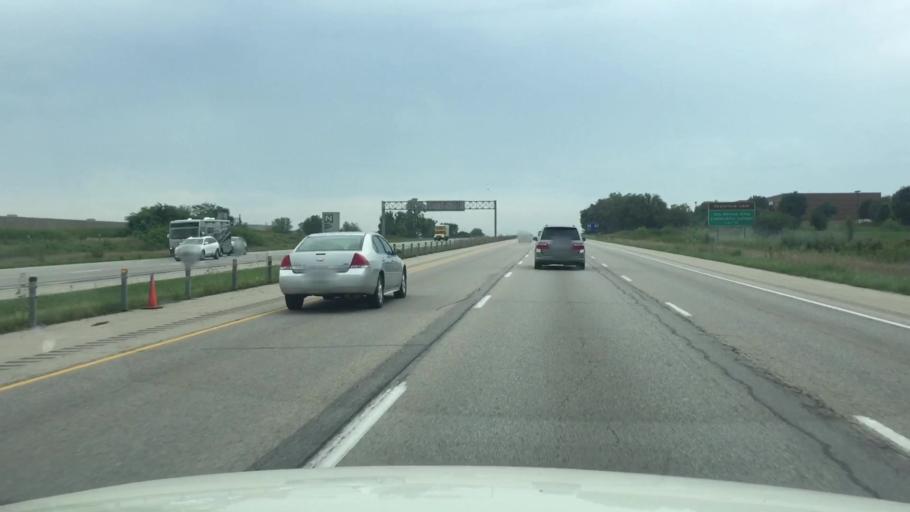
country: US
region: Iowa
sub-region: Polk County
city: Ankeny
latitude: 41.7141
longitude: -93.5766
